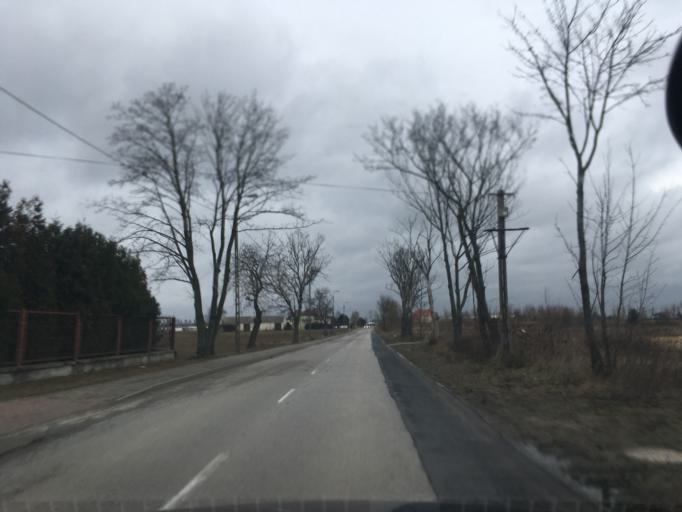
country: PL
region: Masovian Voivodeship
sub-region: Powiat piaseczynski
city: Lesznowola
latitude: 52.1167
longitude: 20.9306
